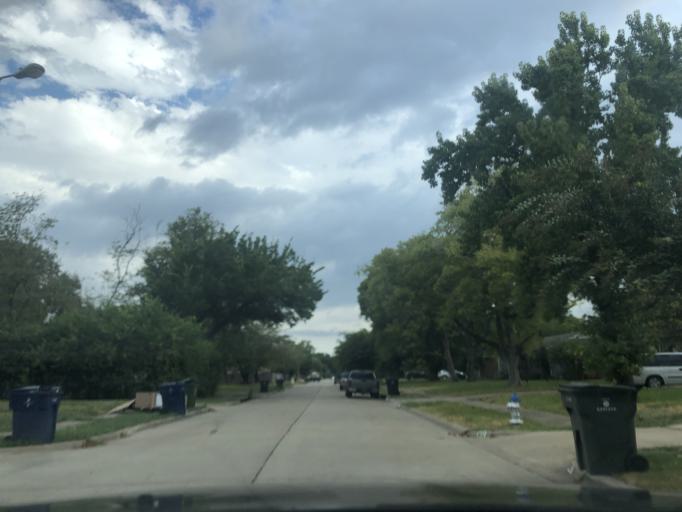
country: US
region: Texas
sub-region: Dallas County
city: Garland
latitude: 32.8800
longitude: -96.6523
